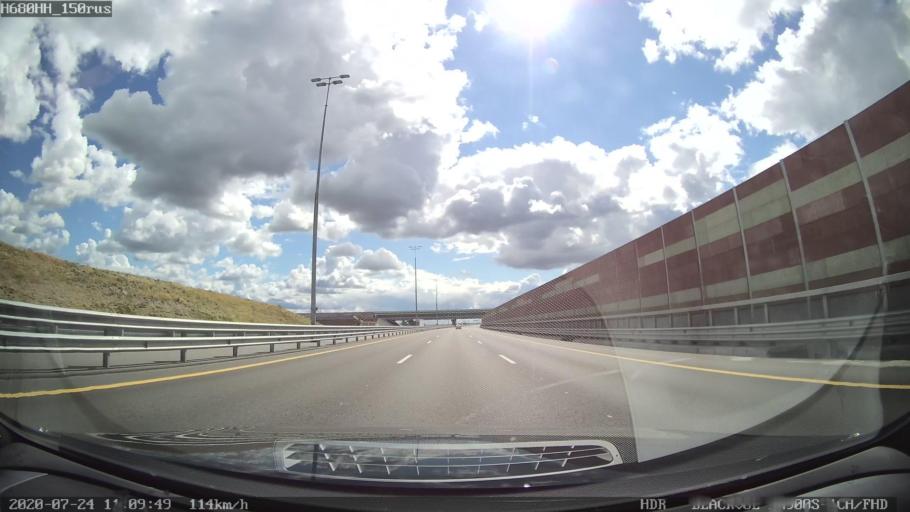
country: RU
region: St.-Petersburg
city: Tyarlevo
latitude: 59.7463
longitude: 30.4848
